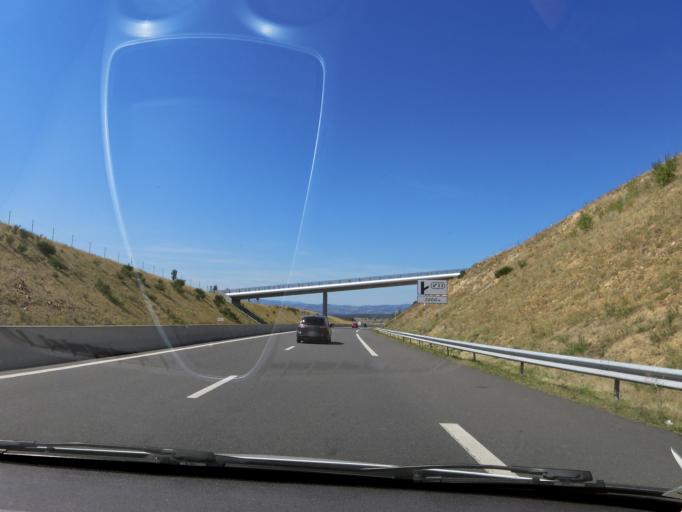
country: FR
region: Rhone-Alpes
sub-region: Departement de la Loire
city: Balbigny
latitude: 45.8393
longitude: 4.1950
